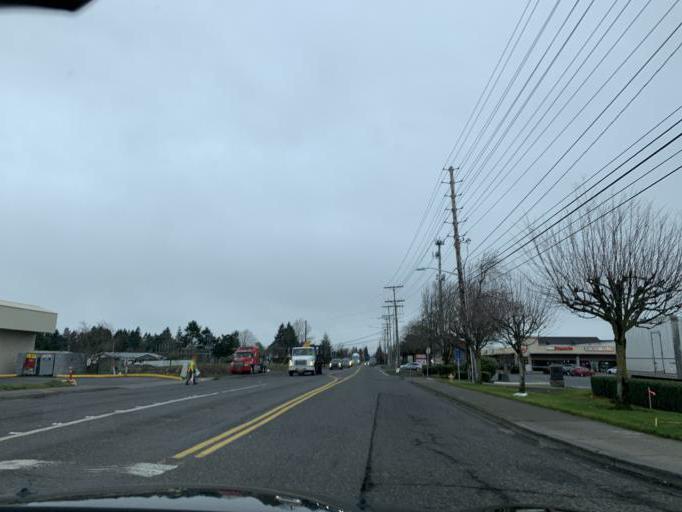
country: US
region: Washington
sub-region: Clark County
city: Mill Plain
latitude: 45.6212
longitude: -122.5041
